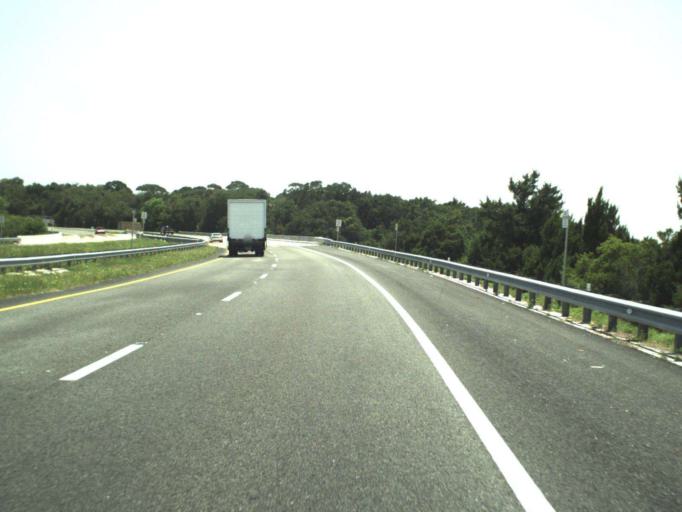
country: US
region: Florida
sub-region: Volusia County
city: Ponce Inlet
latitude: 29.0851
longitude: -80.9680
